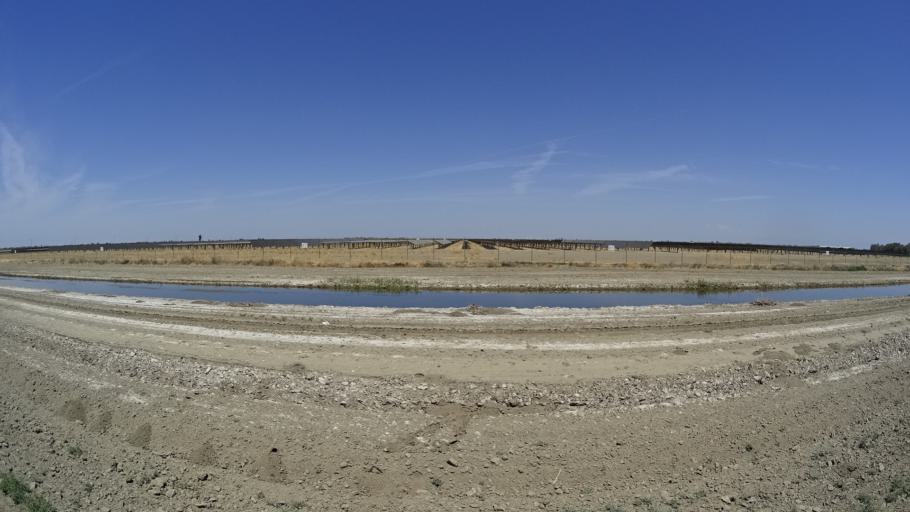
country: US
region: California
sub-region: Kings County
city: Stratford
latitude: 36.2406
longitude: -119.8279
